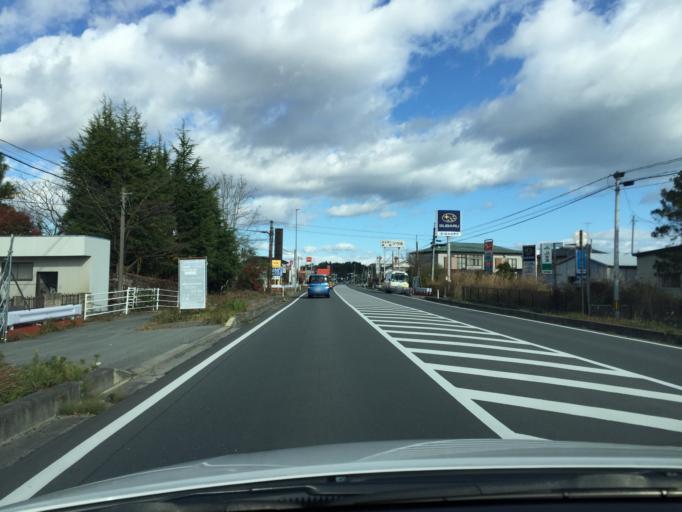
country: JP
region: Fukushima
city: Namie
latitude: 37.4504
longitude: 141.0091
